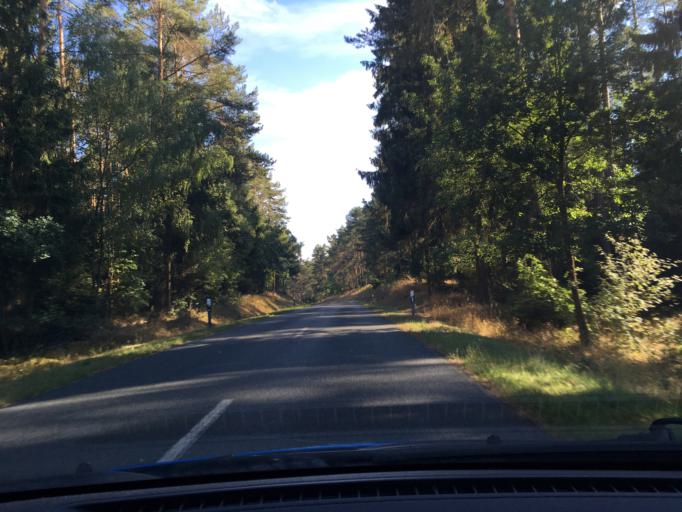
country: DE
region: Lower Saxony
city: Thomasburg
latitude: 53.2376
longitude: 10.7043
